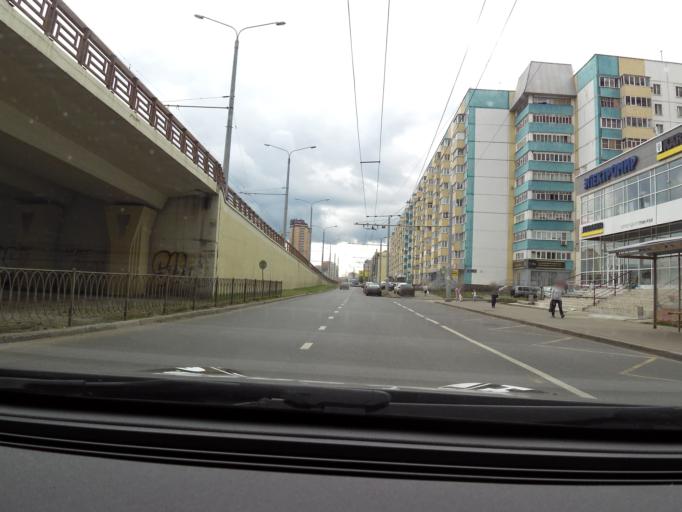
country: RU
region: Tatarstan
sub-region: Gorod Kazan'
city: Kazan
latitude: 55.8196
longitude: 49.1325
